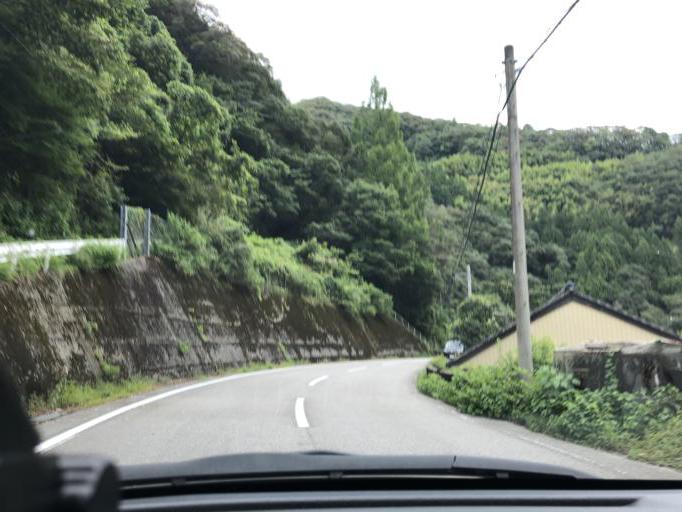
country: JP
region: Kochi
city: Kochi-shi
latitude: 33.6342
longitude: 133.5196
